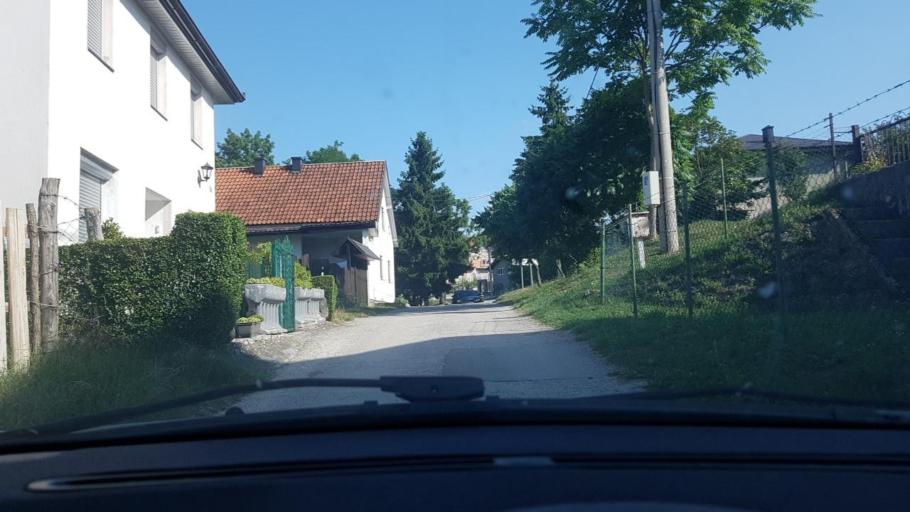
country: BA
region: Federation of Bosnia and Herzegovina
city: Ostrozac
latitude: 44.9065
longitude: 15.9373
